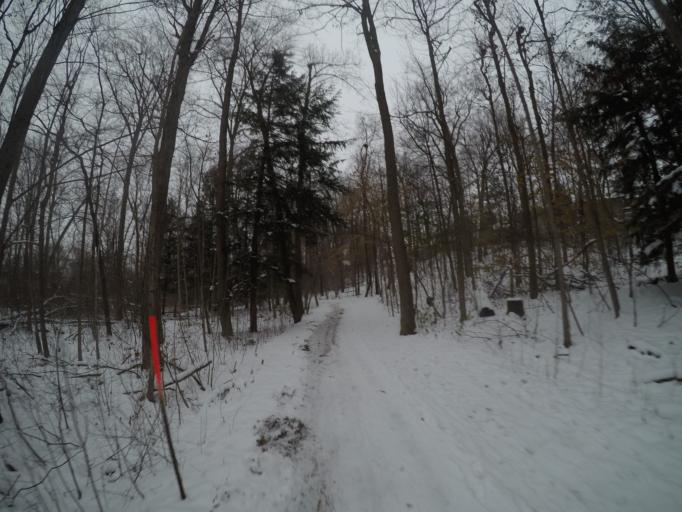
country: CA
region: Ontario
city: Waterloo
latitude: 43.4868
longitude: -80.5100
